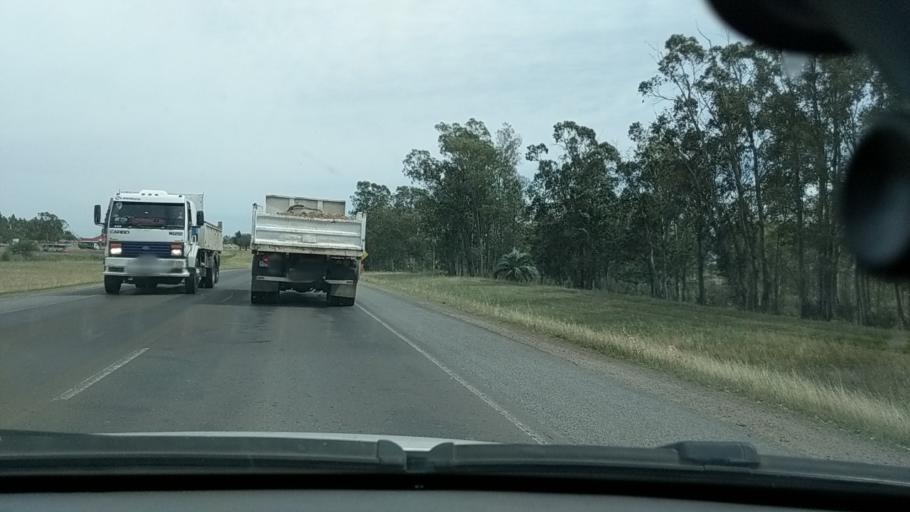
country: UY
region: Durazno
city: Durazno
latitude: -33.4265
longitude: -56.4984
